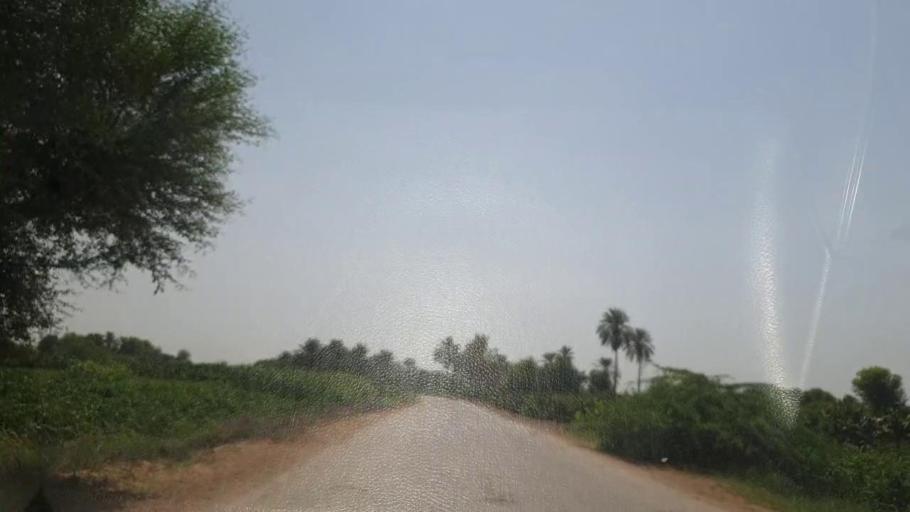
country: PK
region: Sindh
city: Kot Diji
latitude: 27.2803
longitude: 68.6462
